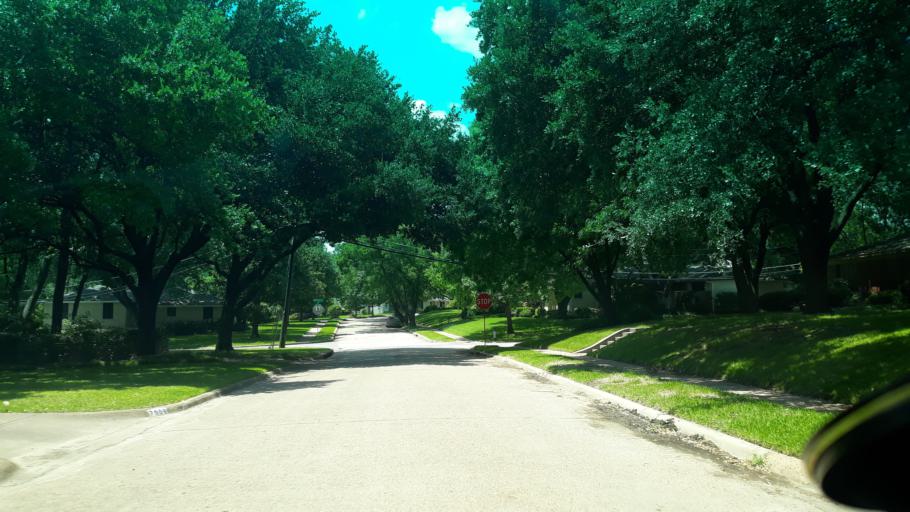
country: US
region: Texas
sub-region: Dallas County
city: Highland Park
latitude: 32.8275
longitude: -96.7394
